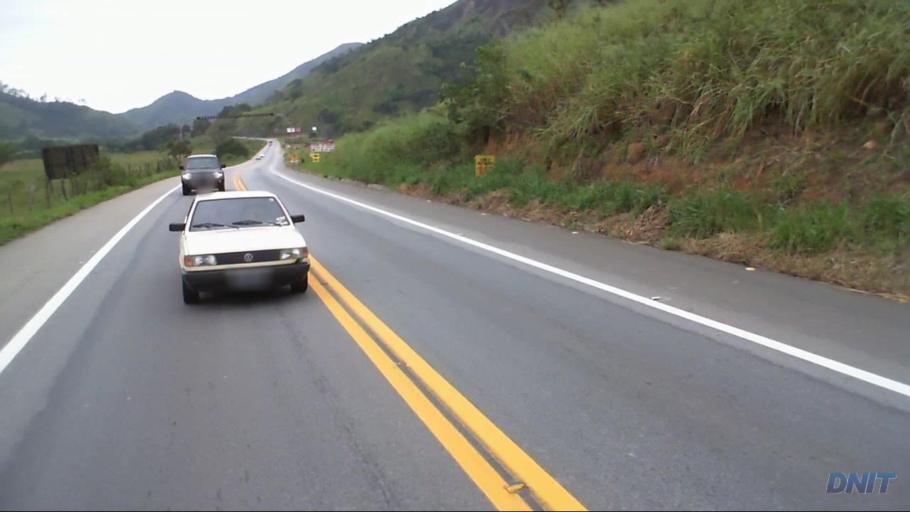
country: BR
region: Minas Gerais
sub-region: Timoteo
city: Timoteo
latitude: -19.5887
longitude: -42.7345
